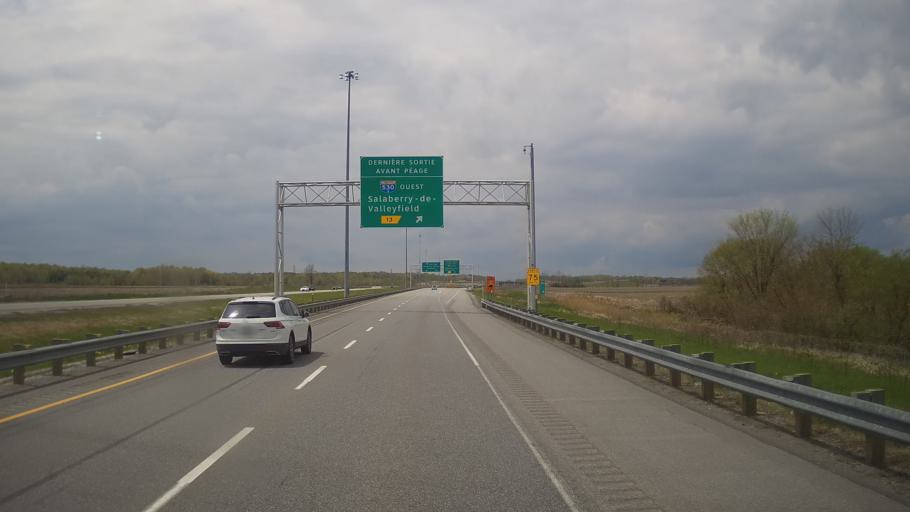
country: CA
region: Quebec
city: Les Cedres
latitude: 45.2962
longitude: -73.9895
